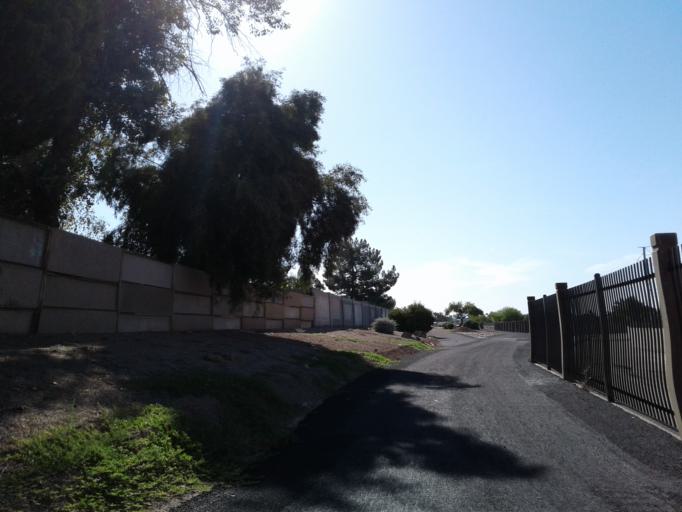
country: US
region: Arizona
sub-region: Maricopa County
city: Glendale
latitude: 33.5898
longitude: -112.1621
